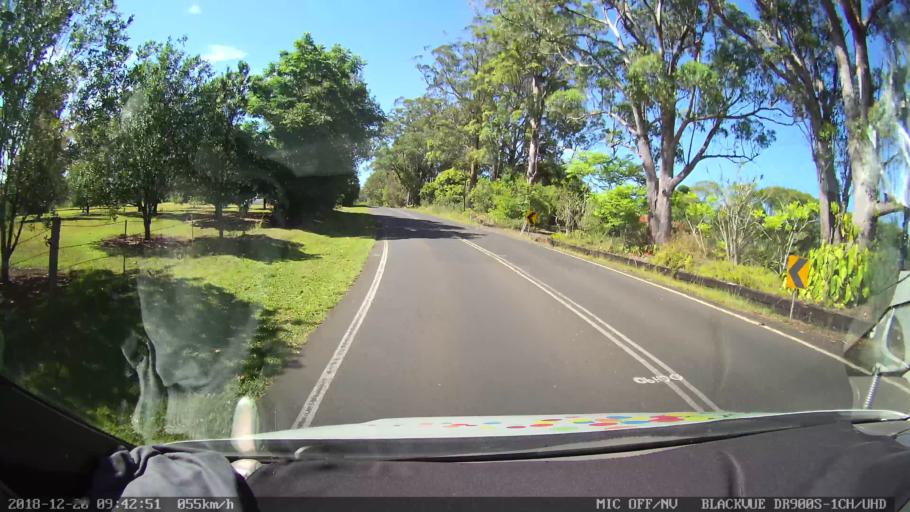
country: AU
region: New South Wales
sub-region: Lismore Municipality
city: Lismore
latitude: -28.7204
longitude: 153.2948
